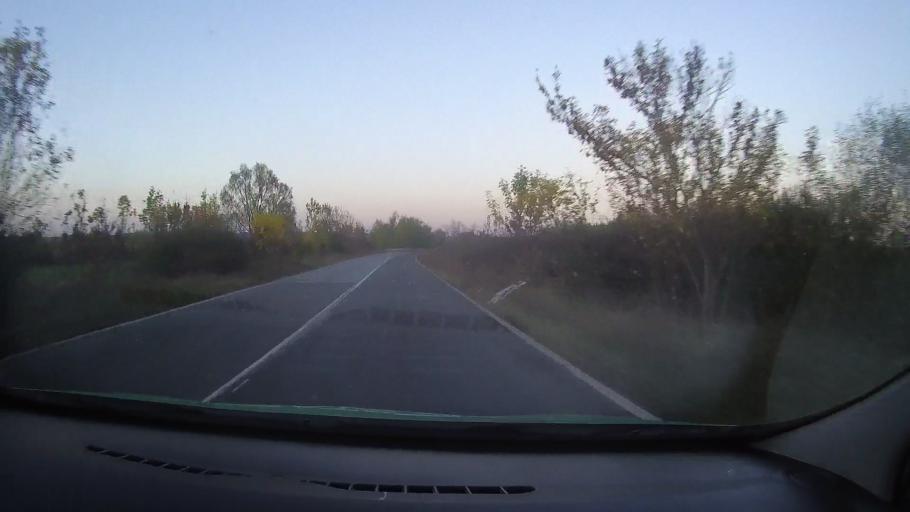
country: RO
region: Timis
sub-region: Comuna Dumbrava
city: Dumbrava
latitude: 45.8391
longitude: 22.1428
